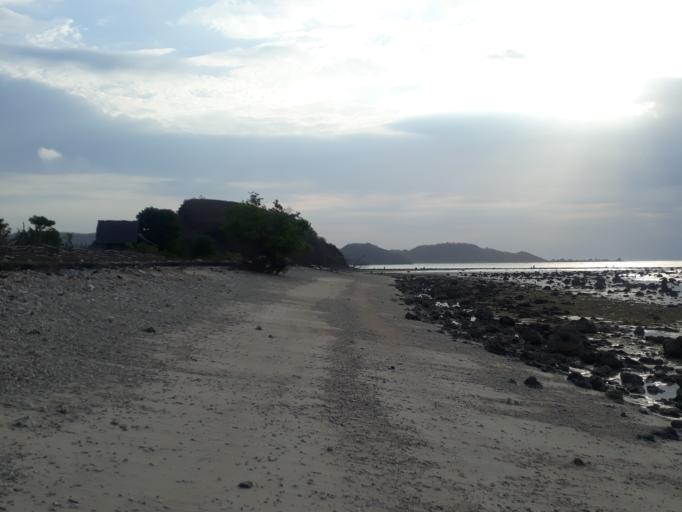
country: ID
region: West Nusa Tenggara
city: Tawun
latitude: -8.7318
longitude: 115.8874
